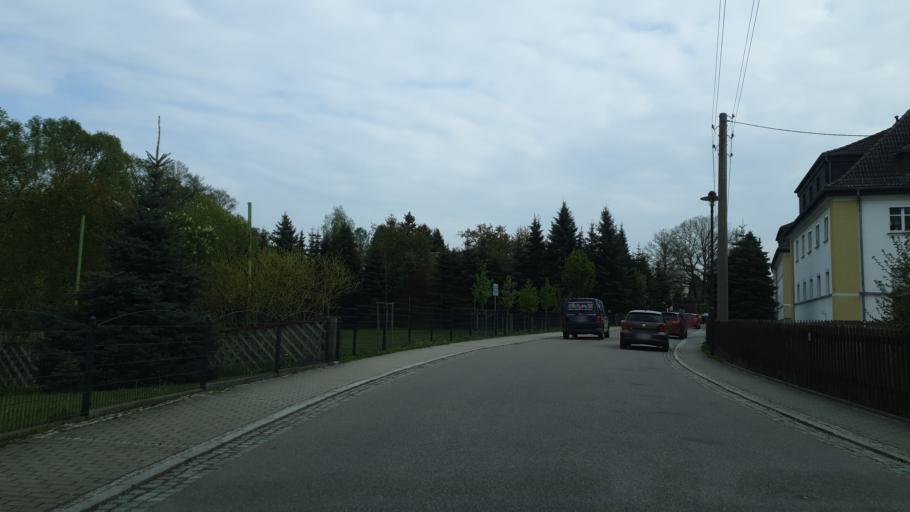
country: DE
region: Saxony
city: Oberlungwitz
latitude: 50.7807
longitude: 12.7100
